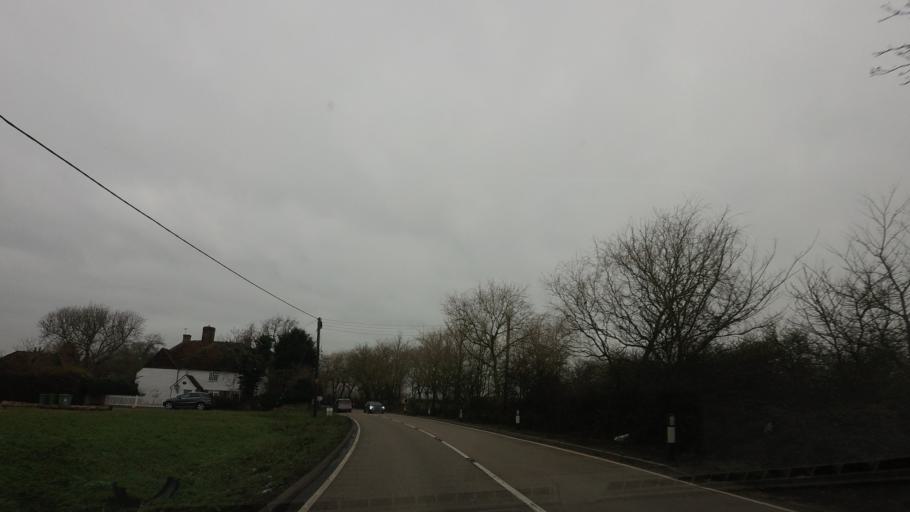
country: GB
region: England
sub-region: Kent
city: Staplehurst
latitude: 51.1904
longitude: 0.5438
